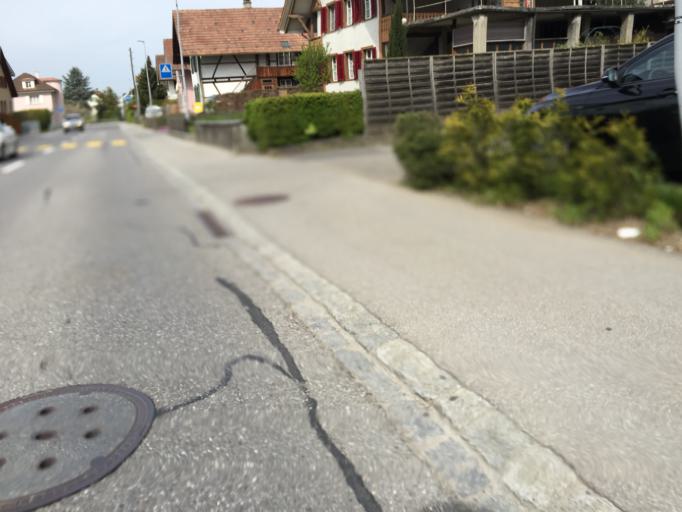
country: CH
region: Fribourg
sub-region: Sense District
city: Flamatt
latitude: 46.8944
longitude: 7.3089
